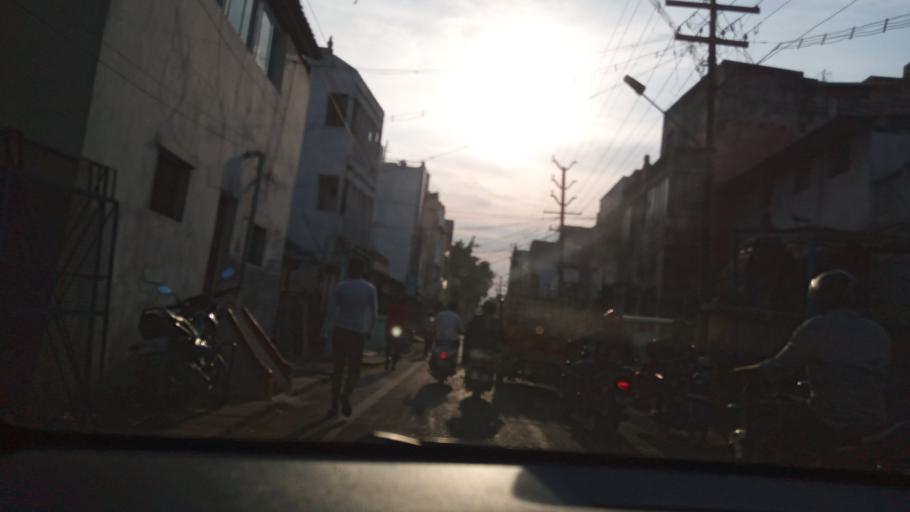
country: IN
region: Tamil Nadu
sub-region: Coimbatore
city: Coimbatore
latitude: 10.9920
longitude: 76.9535
